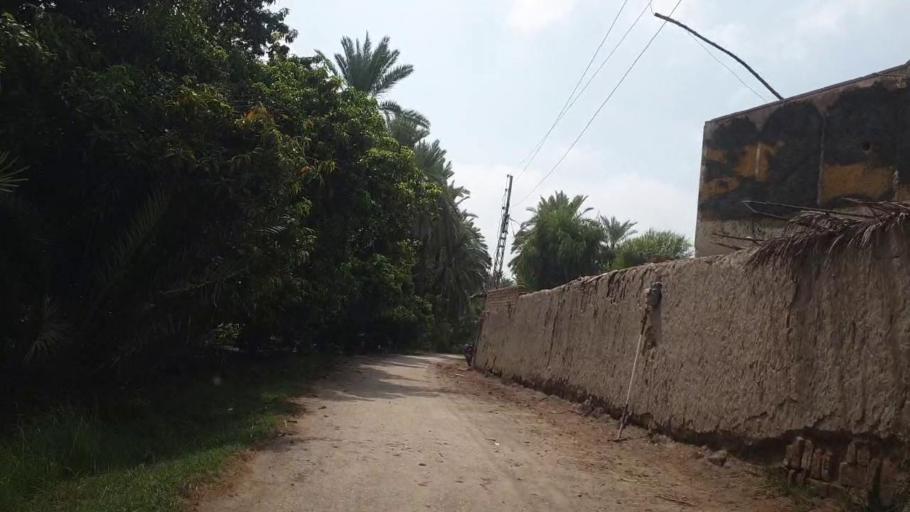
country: PK
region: Sindh
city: Pir jo Goth
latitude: 27.6179
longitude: 68.6752
